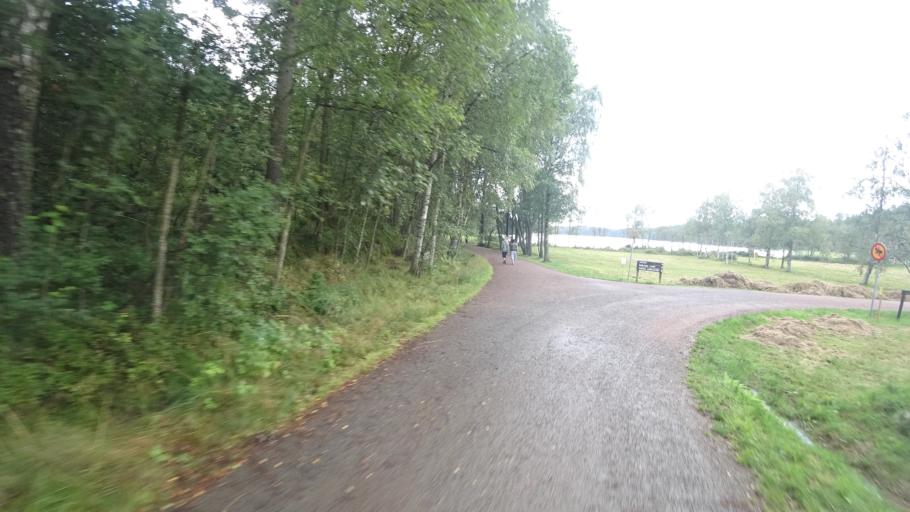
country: SE
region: Vaestra Goetaland
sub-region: Partille Kommun
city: Ojersjo
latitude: 57.6842
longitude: 12.0848
